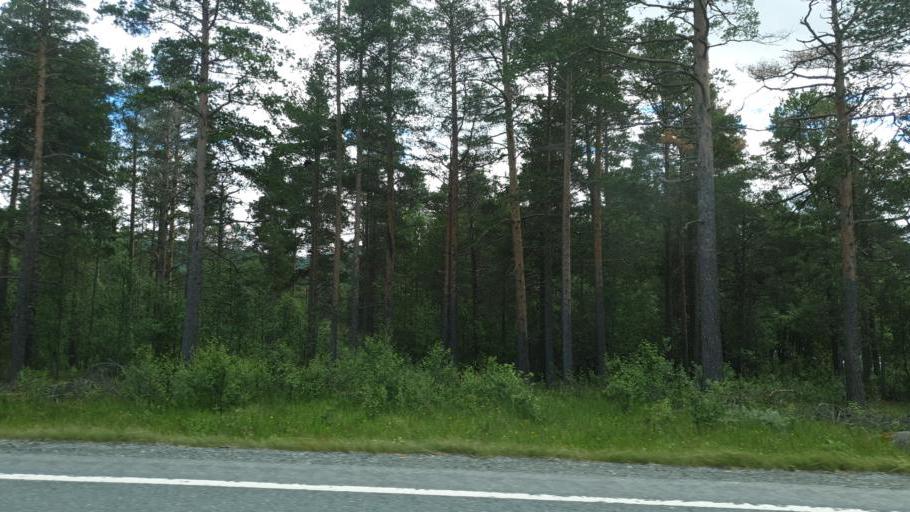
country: NO
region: Sor-Trondelag
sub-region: Oppdal
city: Oppdal
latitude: 62.6502
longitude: 9.8579
